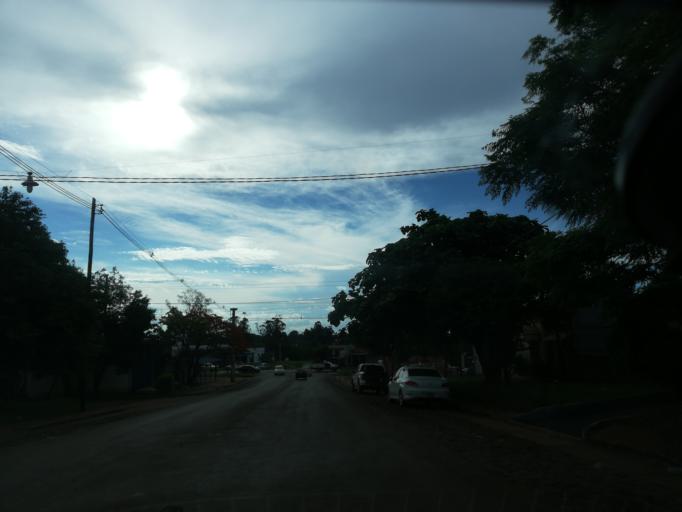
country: AR
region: Misiones
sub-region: Departamento de Capital
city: Posadas
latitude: -27.4189
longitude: -55.9294
